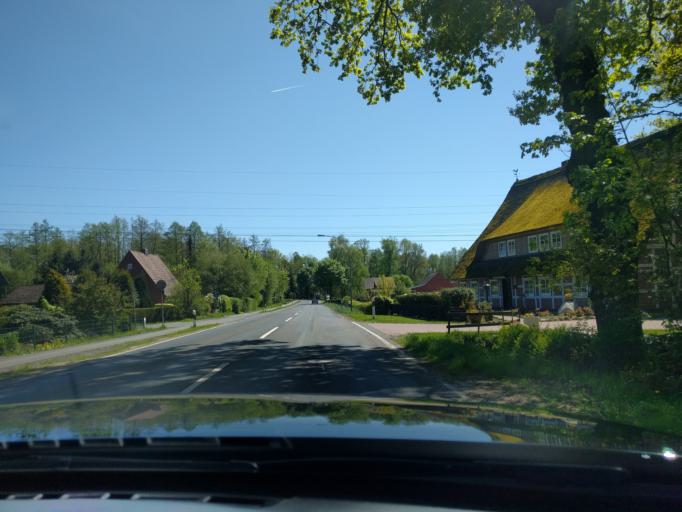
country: DE
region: Lower Saxony
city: Seevetal
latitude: 53.3987
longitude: 10.0086
